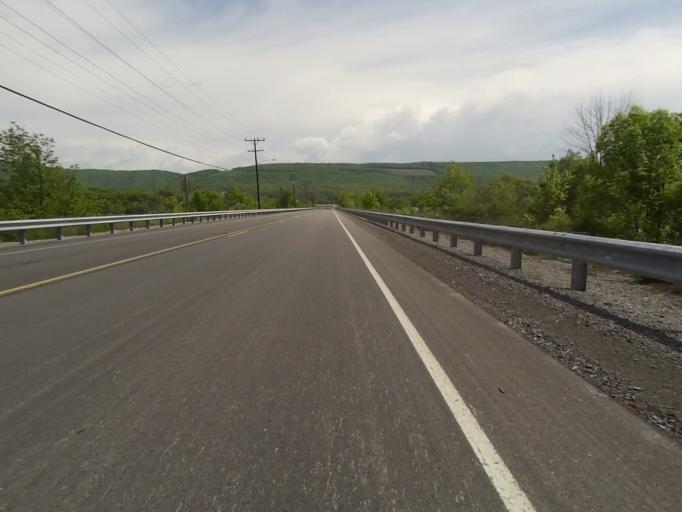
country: US
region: Pennsylvania
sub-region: Centre County
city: Zion
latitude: 41.0212
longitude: -77.6692
